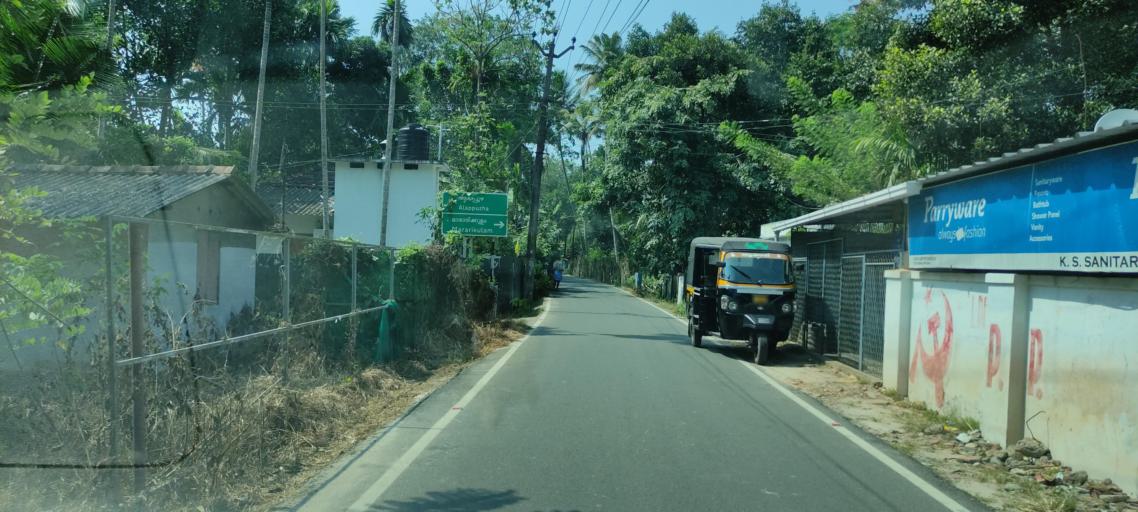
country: IN
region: Kerala
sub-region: Alappuzha
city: Alleppey
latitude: 9.5550
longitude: 76.3124
